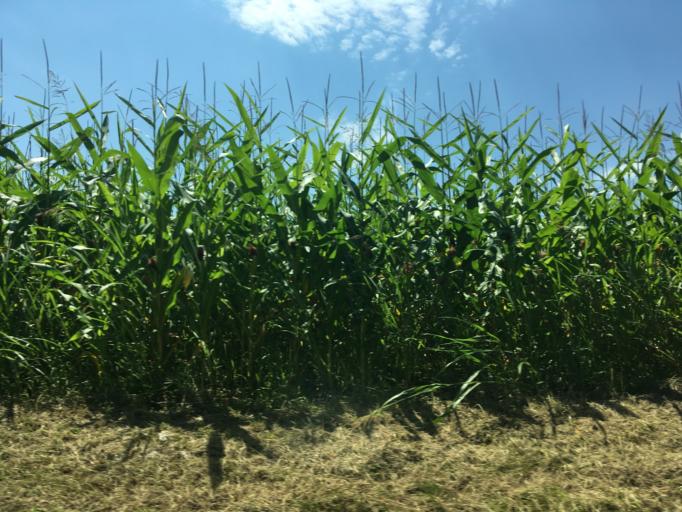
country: SI
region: Metlika
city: Metlika
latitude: 45.5934
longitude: 15.3414
